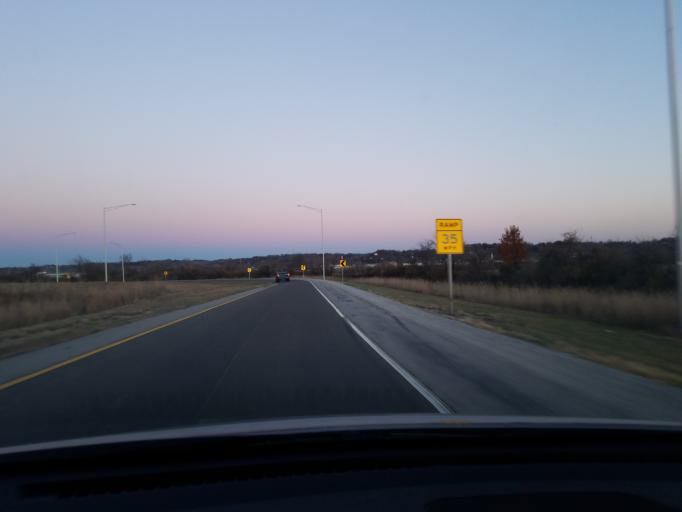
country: US
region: Illinois
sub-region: Saint Clair County
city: Washington Park
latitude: 38.6166
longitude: -90.0681
